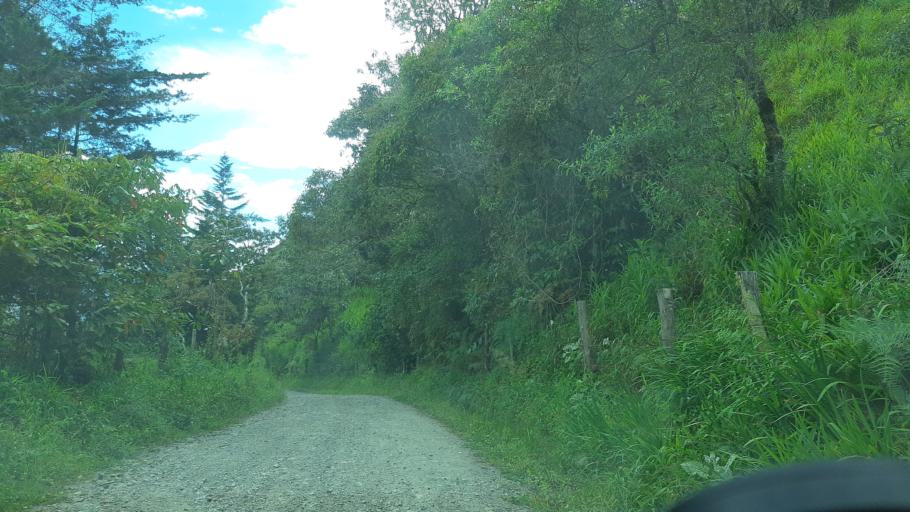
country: CO
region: Boyaca
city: Garagoa
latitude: 5.0518
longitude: -73.3526
